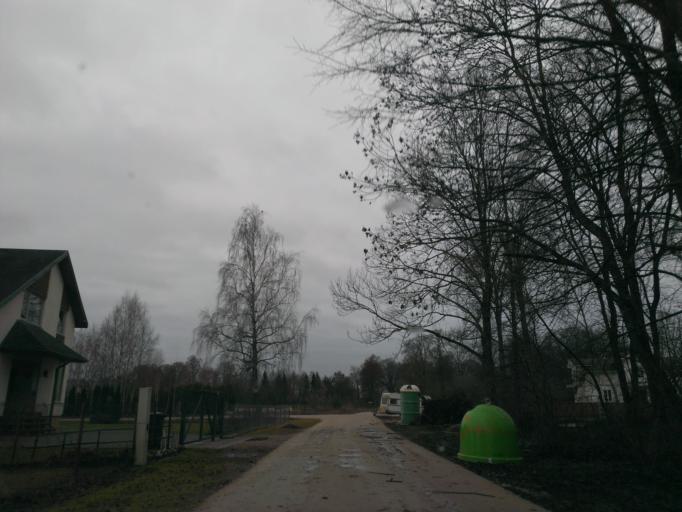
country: LV
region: Adazi
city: Adazi
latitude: 57.0762
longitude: 24.3448
